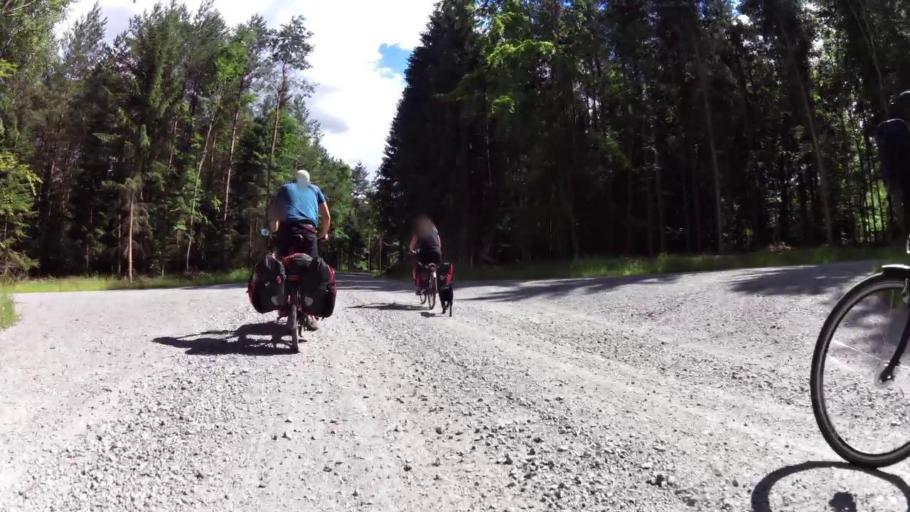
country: PL
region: West Pomeranian Voivodeship
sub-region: Powiat lobeski
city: Lobez
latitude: 53.6791
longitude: 15.5518
